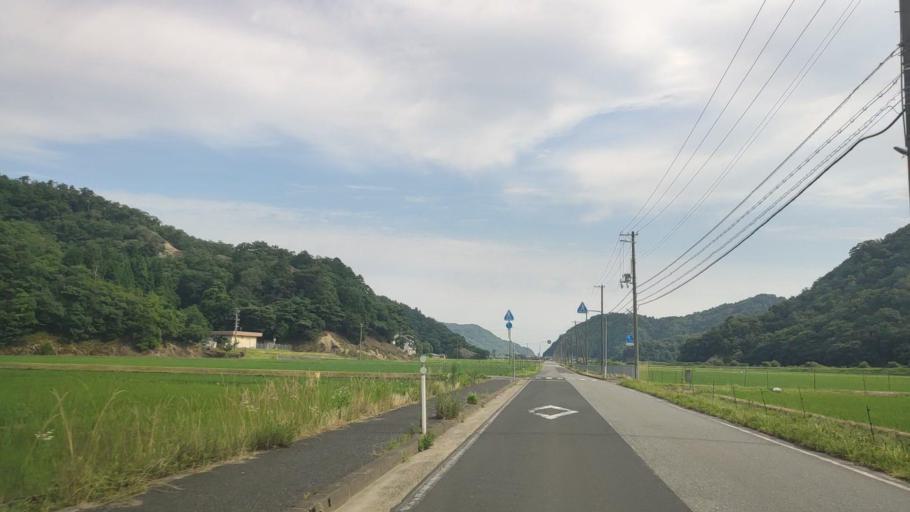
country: JP
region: Hyogo
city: Toyooka
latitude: 35.6228
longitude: 134.8413
